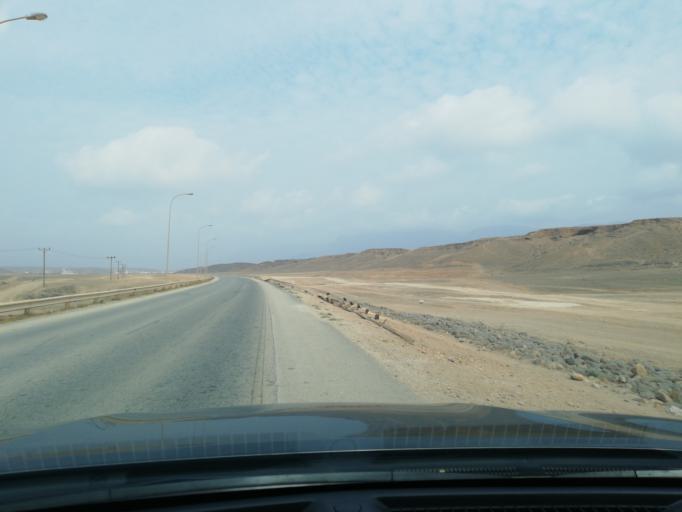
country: OM
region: Zufar
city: Salalah
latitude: 16.9604
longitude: 53.8911
